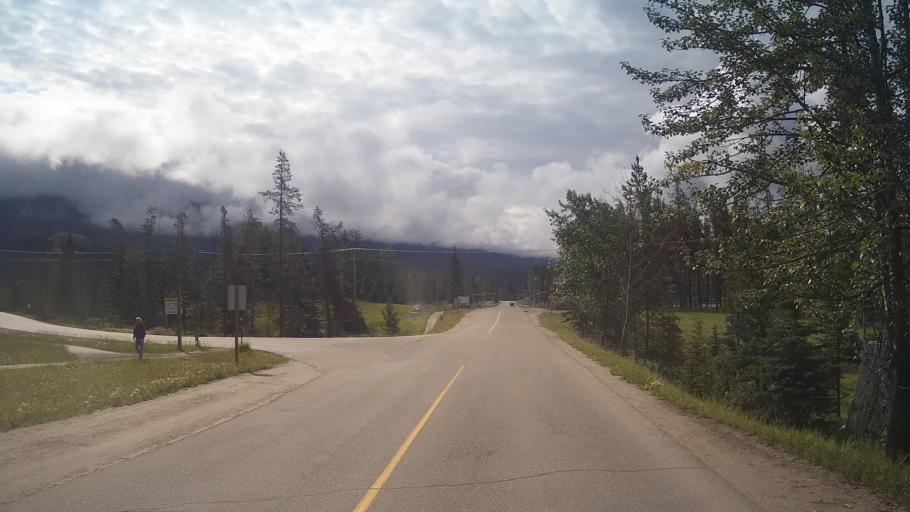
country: CA
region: Alberta
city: Jasper Park Lodge
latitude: 52.8713
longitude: -118.0794
